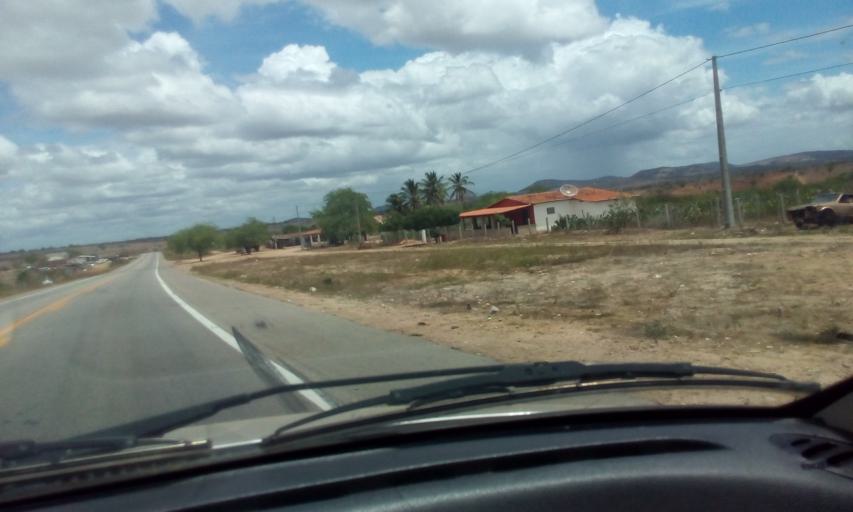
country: BR
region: Rio Grande do Norte
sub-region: Tangara
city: Tangara
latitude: -6.1896
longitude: -35.7869
